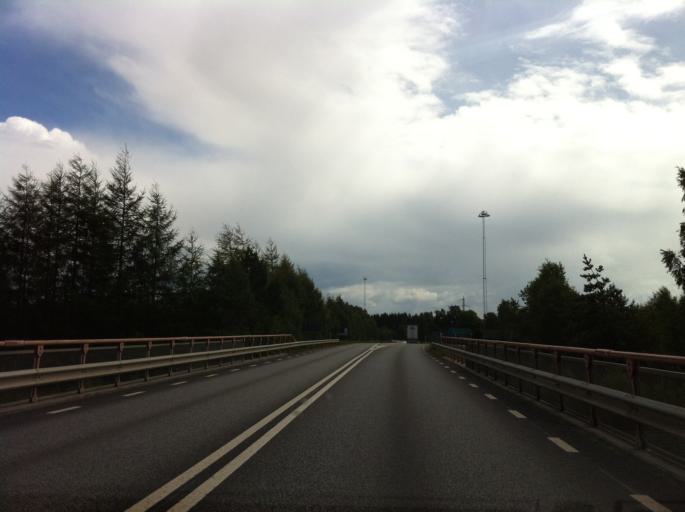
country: SE
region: Skane
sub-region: Hassleholms Kommun
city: Bjarnum
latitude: 56.2020
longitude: 13.6605
